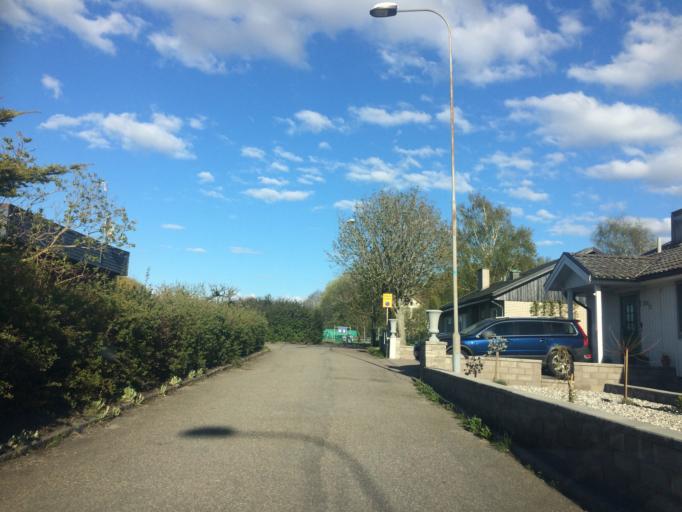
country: SE
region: Vaestra Goetaland
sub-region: Goteborg
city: Goeteborg
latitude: 57.7585
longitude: 11.9316
